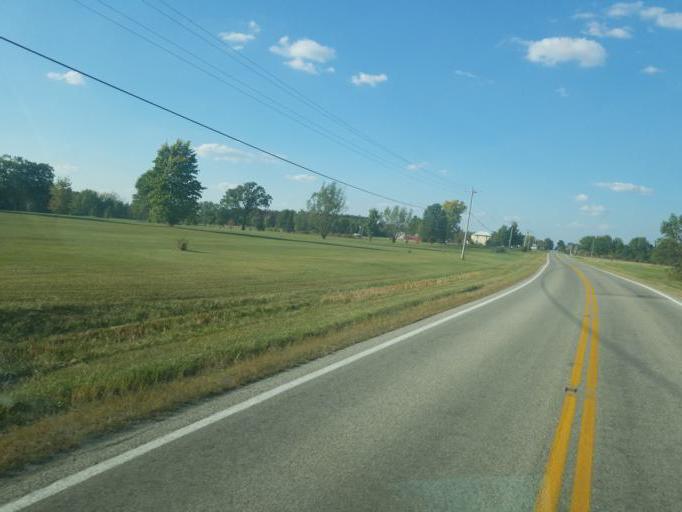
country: US
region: Ohio
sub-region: Union County
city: Richwood
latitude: 40.5740
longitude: -83.3150
